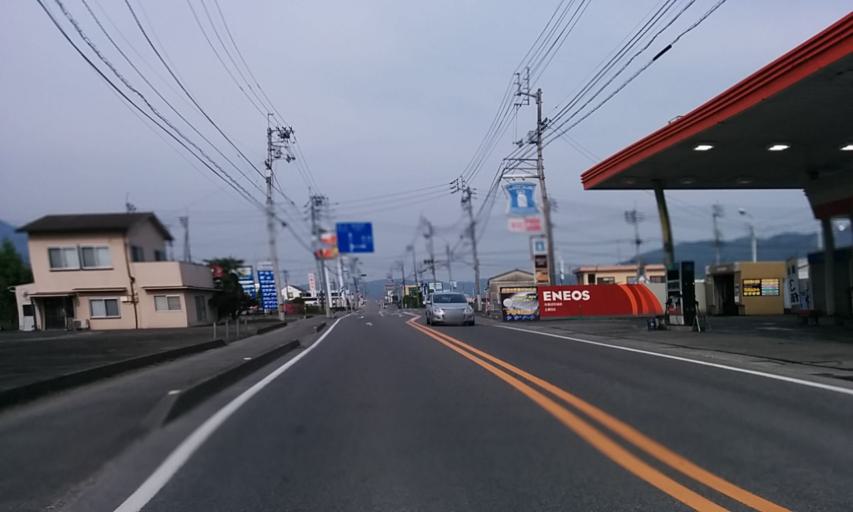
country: JP
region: Ehime
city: Niihama
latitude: 33.9569
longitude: 133.4319
